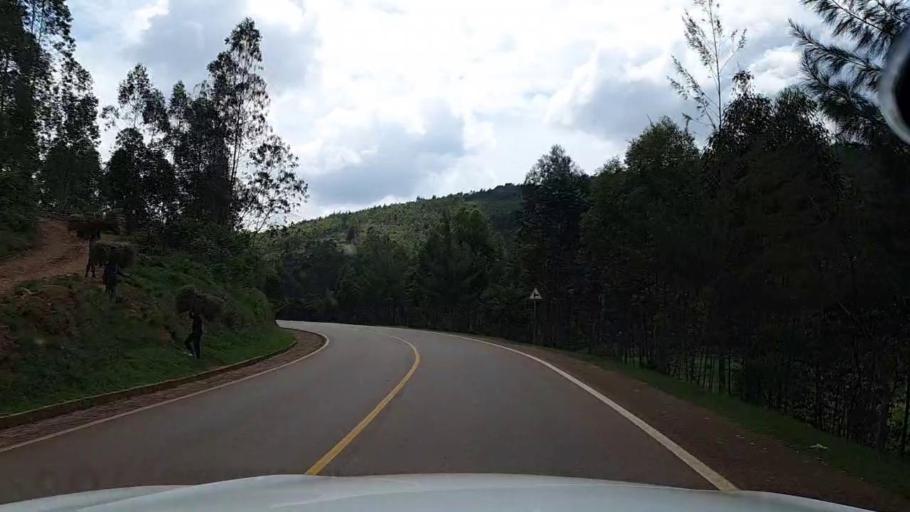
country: RW
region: Kigali
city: Kigali
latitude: -1.8195
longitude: 30.1129
